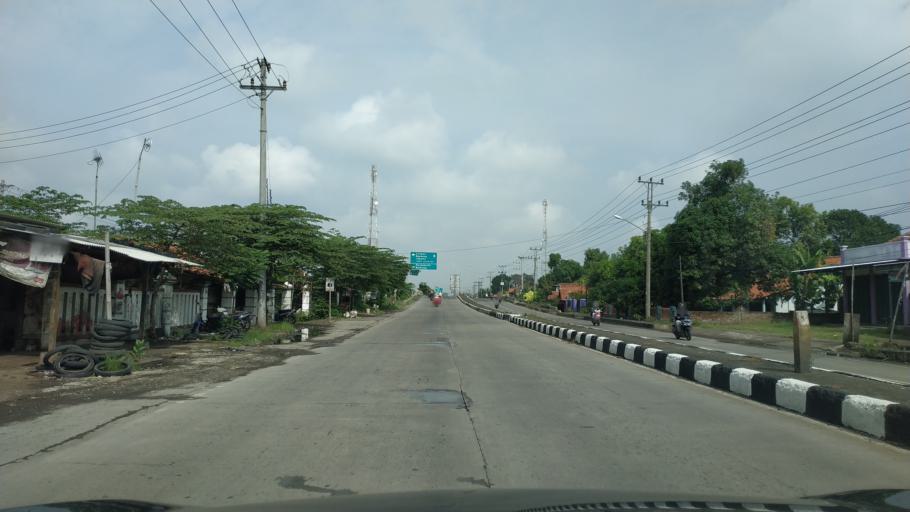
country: ID
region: Central Java
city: Ketanggungan
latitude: -6.8719
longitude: 108.8894
